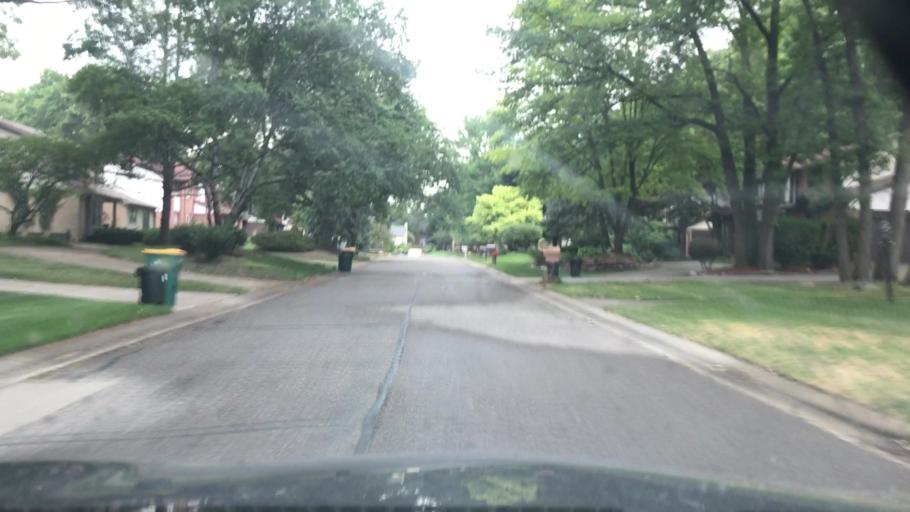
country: US
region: Michigan
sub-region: Oakland County
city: Farmington Hills
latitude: 42.5092
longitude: -83.4039
